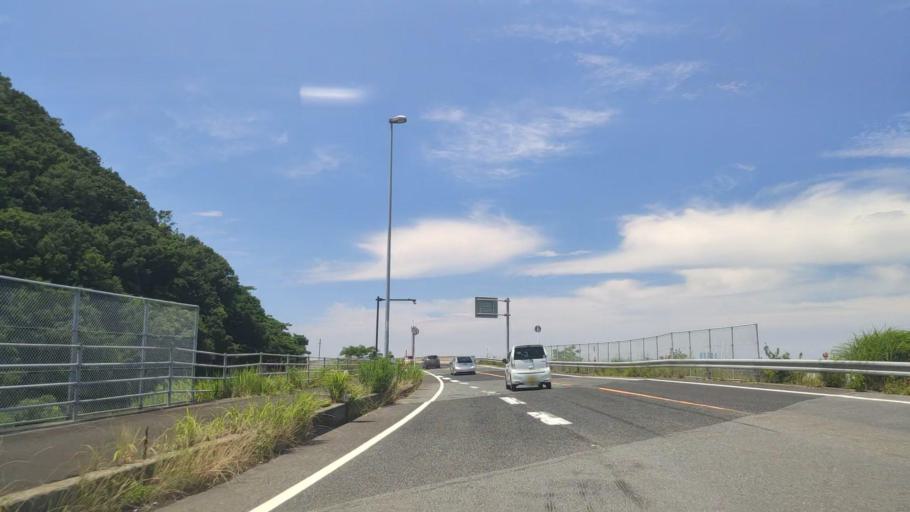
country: JP
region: Tottori
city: Tottori
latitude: 35.4710
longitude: 134.2421
